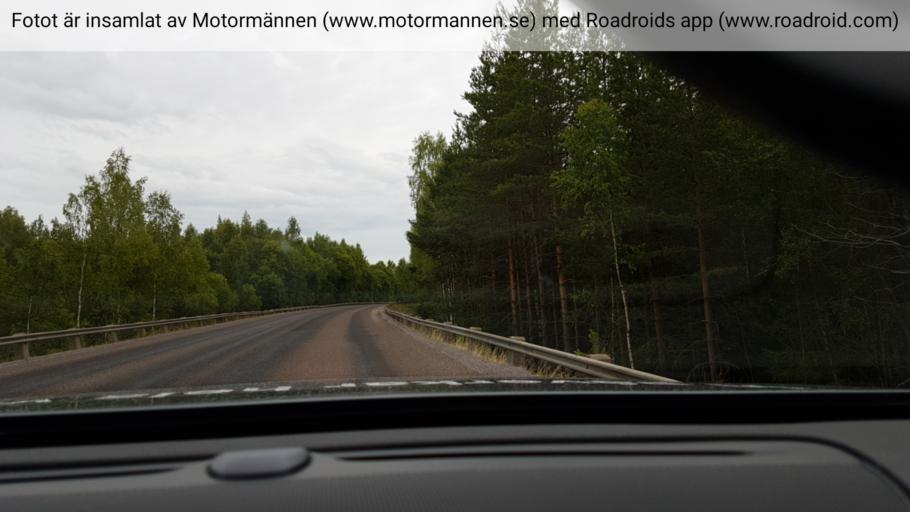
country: SE
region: Dalarna
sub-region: Ludvika Kommun
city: Ludvika
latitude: 60.2955
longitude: 15.2184
